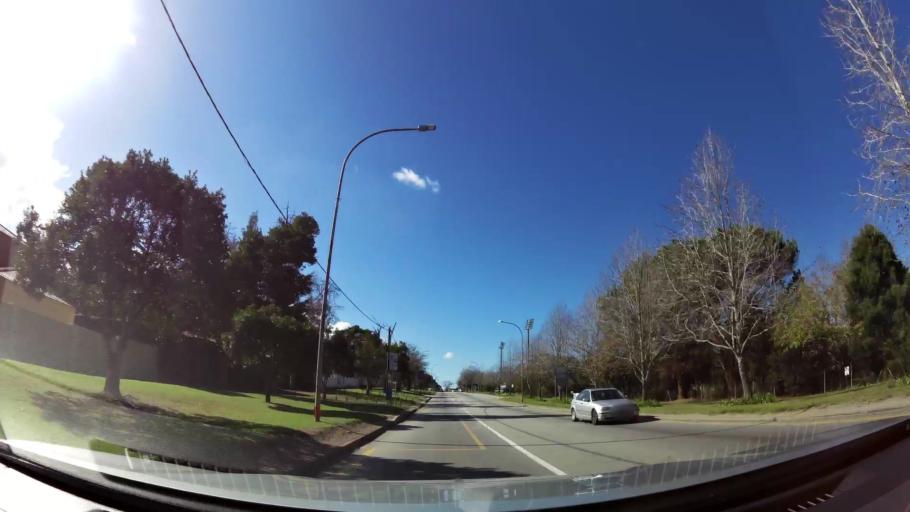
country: ZA
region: Western Cape
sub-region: Eden District Municipality
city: George
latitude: -33.9524
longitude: 22.4444
